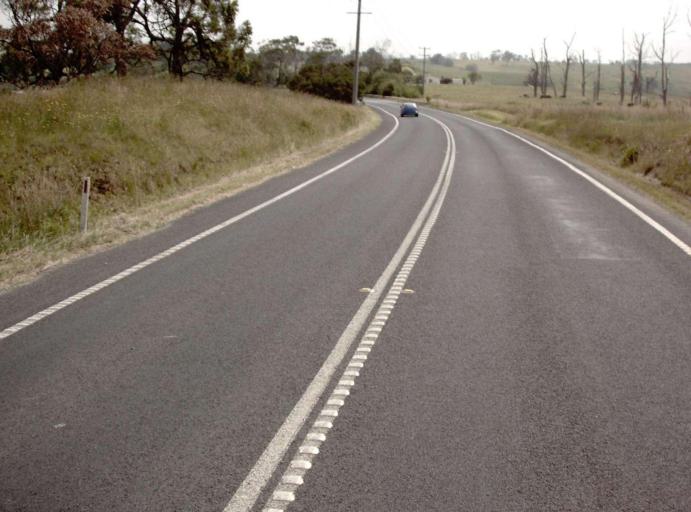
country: AU
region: Victoria
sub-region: Baw Baw
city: Warragul
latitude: -38.4409
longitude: 146.0344
